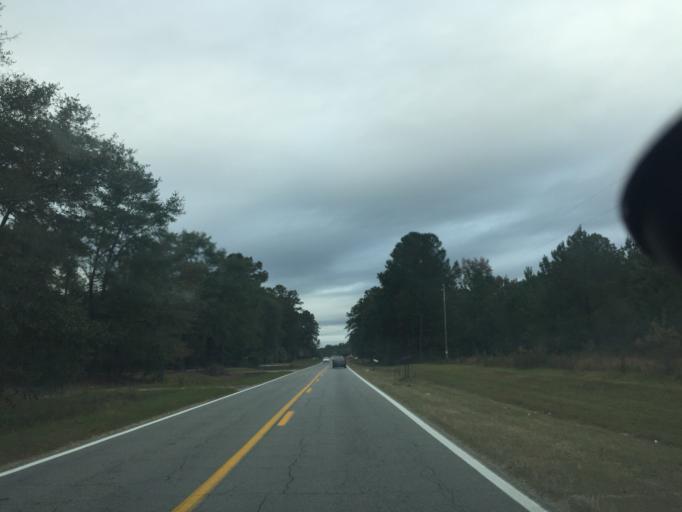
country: US
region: Georgia
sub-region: Chatham County
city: Bloomingdale
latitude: 32.0831
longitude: -81.3720
